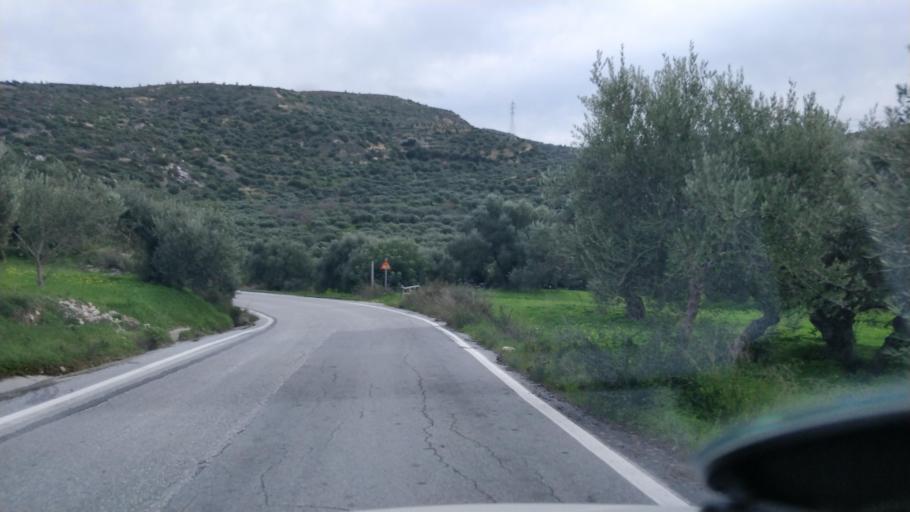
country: GR
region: Crete
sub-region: Nomos Lasithiou
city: Gra Liyia
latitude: 35.0953
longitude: 25.6963
